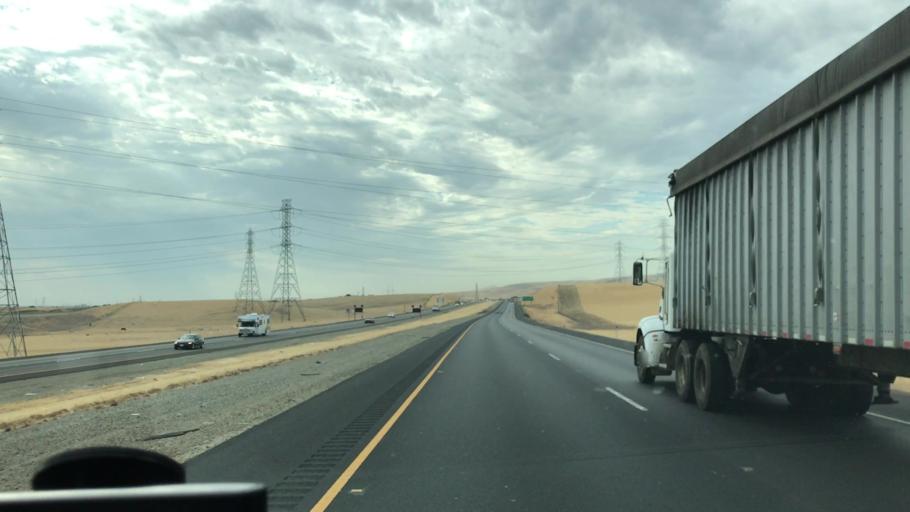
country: US
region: California
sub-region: San Joaquin County
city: Mountain House
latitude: 37.7361
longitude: -121.5540
